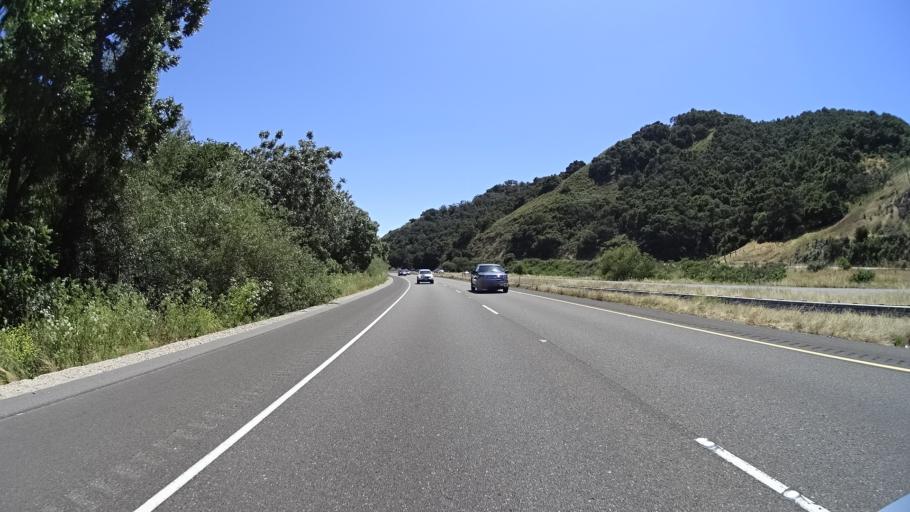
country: US
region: California
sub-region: San Luis Obispo County
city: Avila Beach
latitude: 35.2159
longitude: -120.6958
